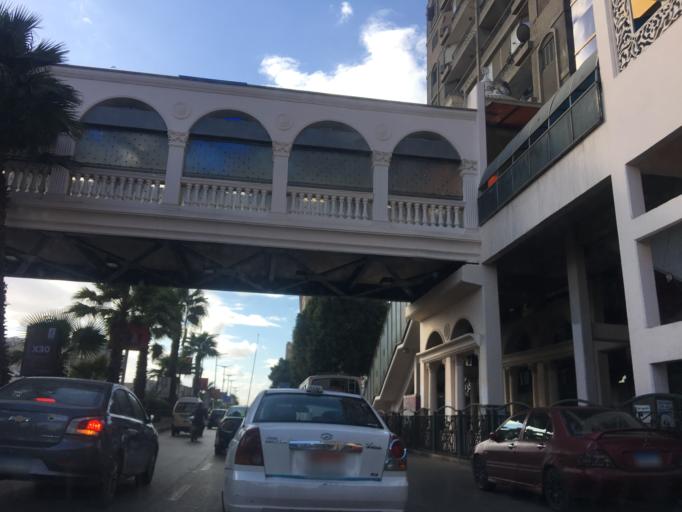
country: EG
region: Al Jizah
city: Al Jizah
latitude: 30.0287
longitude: 31.2061
